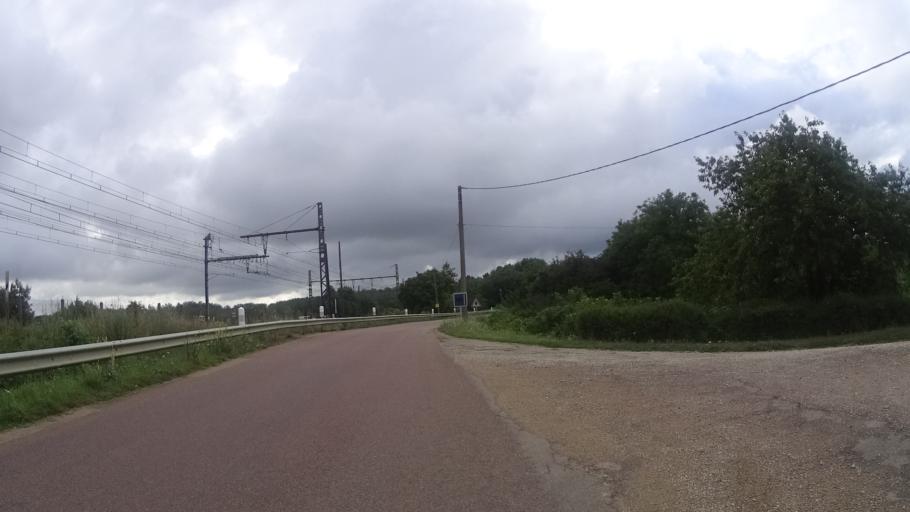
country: FR
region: Bourgogne
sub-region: Departement de l'Yonne
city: Brienon-sur-Armancon
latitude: 47.9795
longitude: 3.6511
